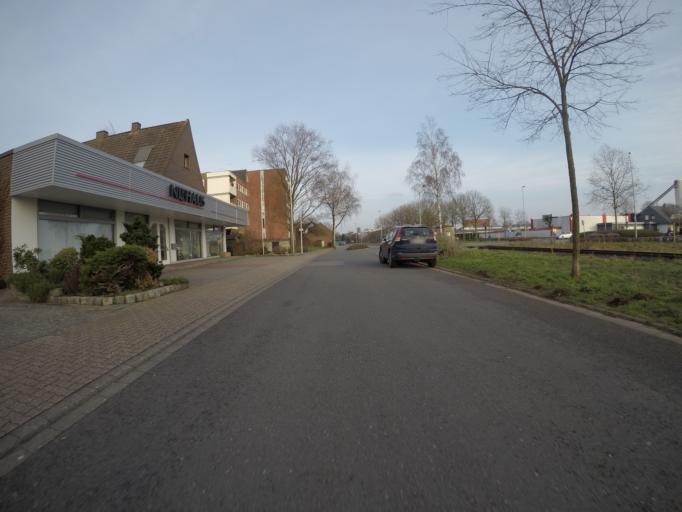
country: DE
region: North Rhine-Westphalia
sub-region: Regierungsbezirk Dusseldorf
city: Bocholt
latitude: 51.8202
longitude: 6.6006
